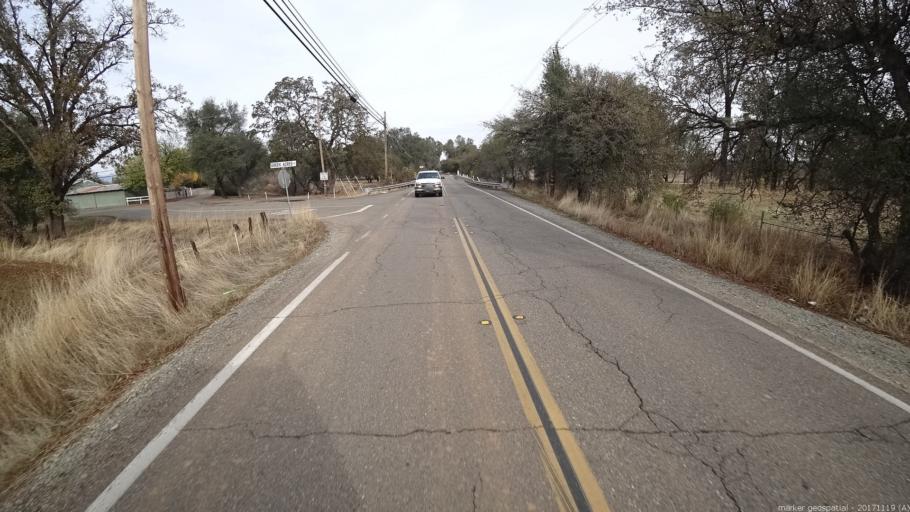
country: US
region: California
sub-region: Shasta County
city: Anderson
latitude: 40.5219
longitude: -122.3337
